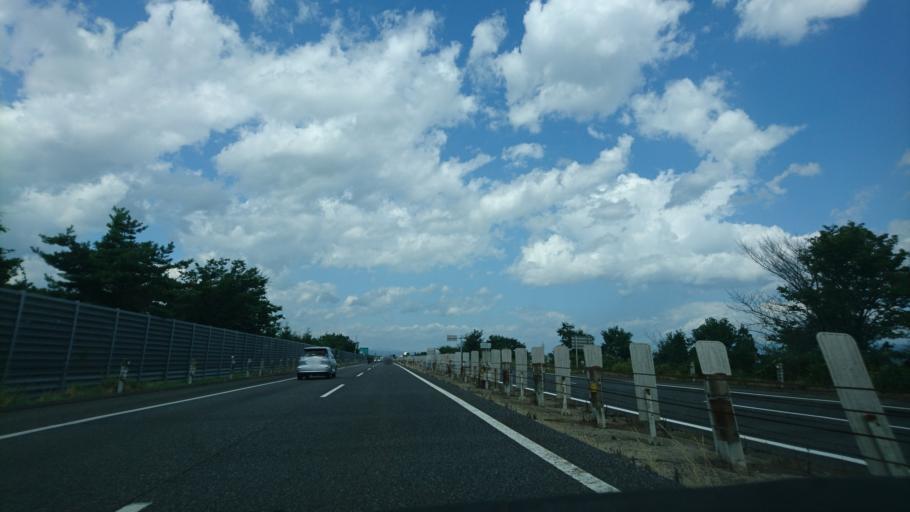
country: JP
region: Iwate
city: Morioka-shi
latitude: 39.6387
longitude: 141.1262
